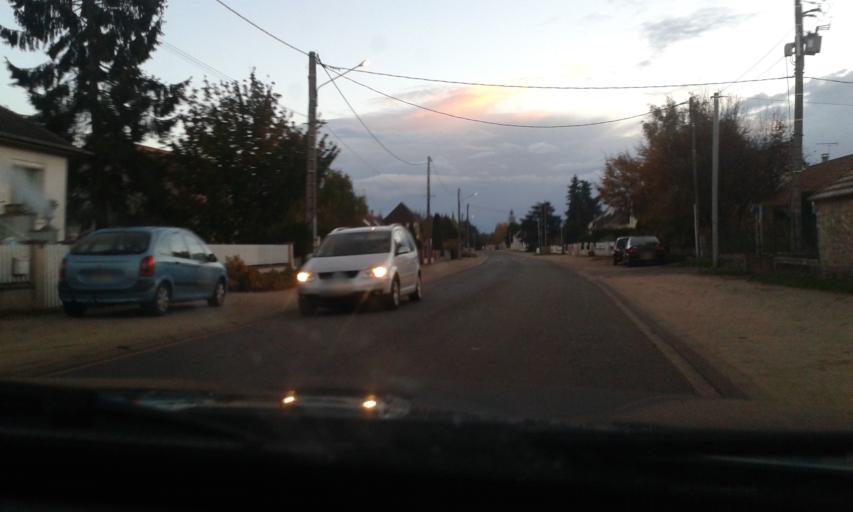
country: FR
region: Centre
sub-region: Departement du Loiret
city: Huisseau-sur-Mauves
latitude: 47.8991
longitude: 1.7044
